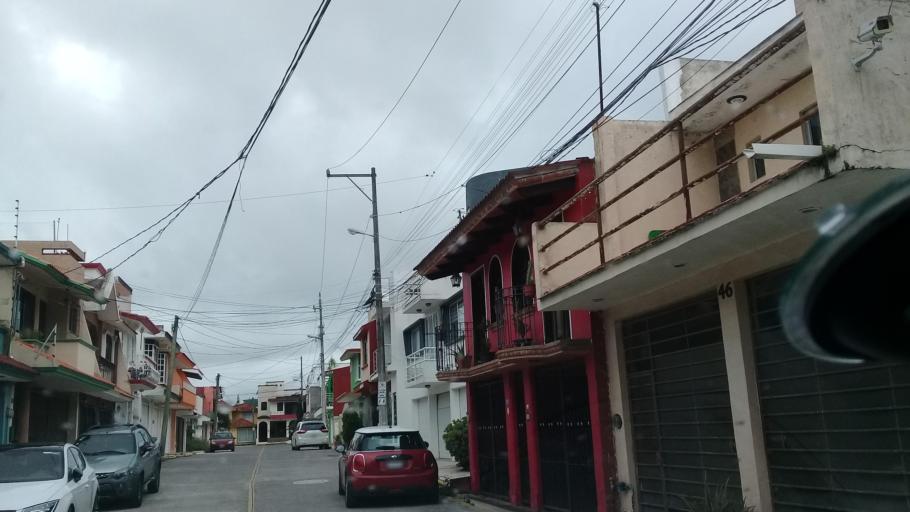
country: MX
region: Veracruz
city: El Castillo
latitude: 19.5339
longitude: -96.8860
